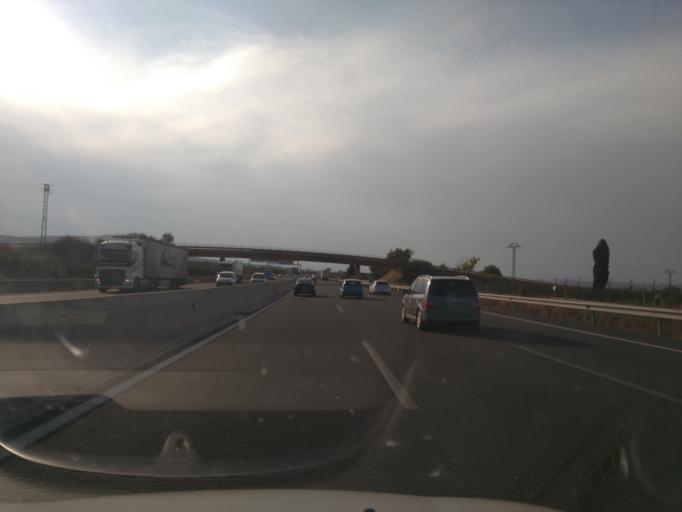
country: ES
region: Valencia
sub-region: Provincia de Valencia
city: Torrent
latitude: 39.4223
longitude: -0.5170
